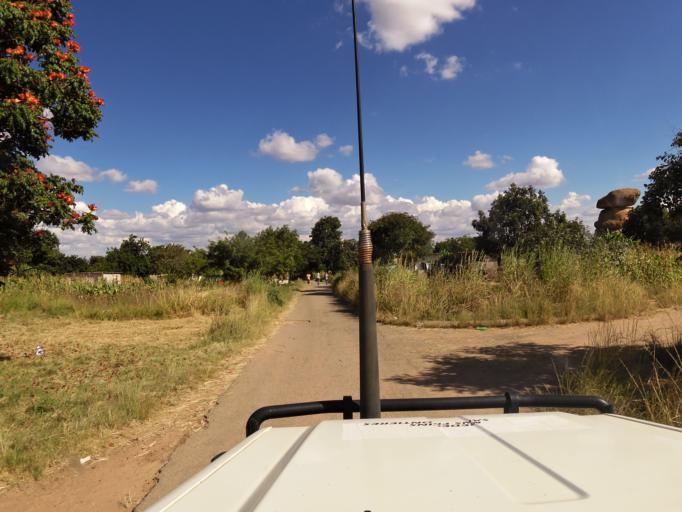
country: ZW
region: Harare
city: Epworth
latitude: -17.8725
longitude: 31.1441
